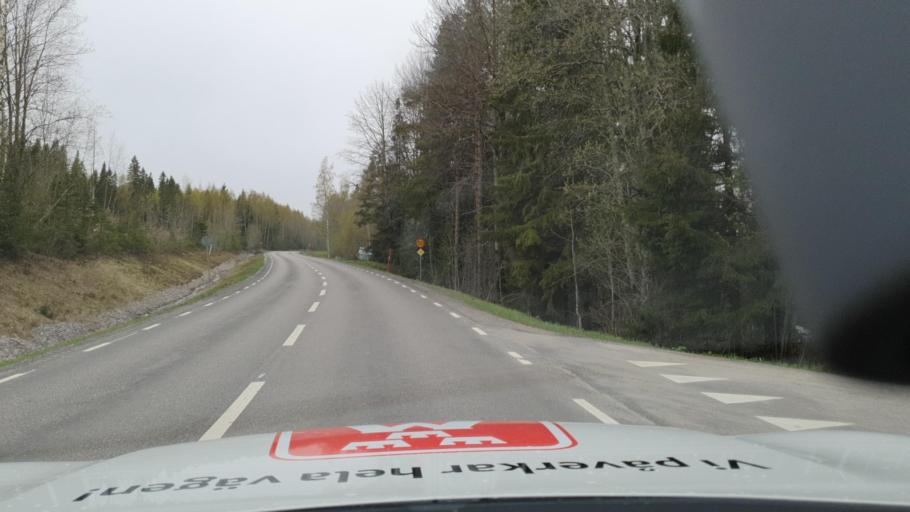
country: SE
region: Vaesterbotten
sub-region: Vannas Kommun
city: Vaennaes
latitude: 63.7852
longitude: 19.8367
